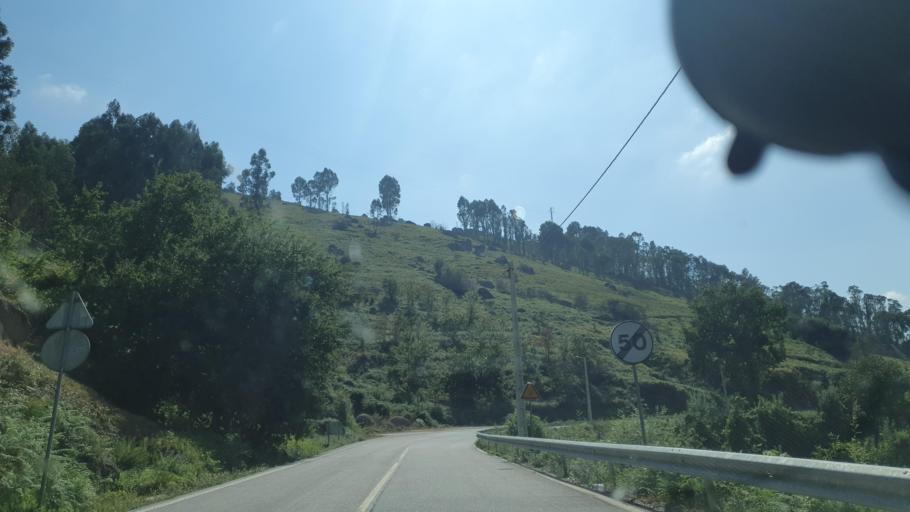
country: PT
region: Braga
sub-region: Vieira do Minho
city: Vieira do Minho
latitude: 41.6723
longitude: -8.1489
